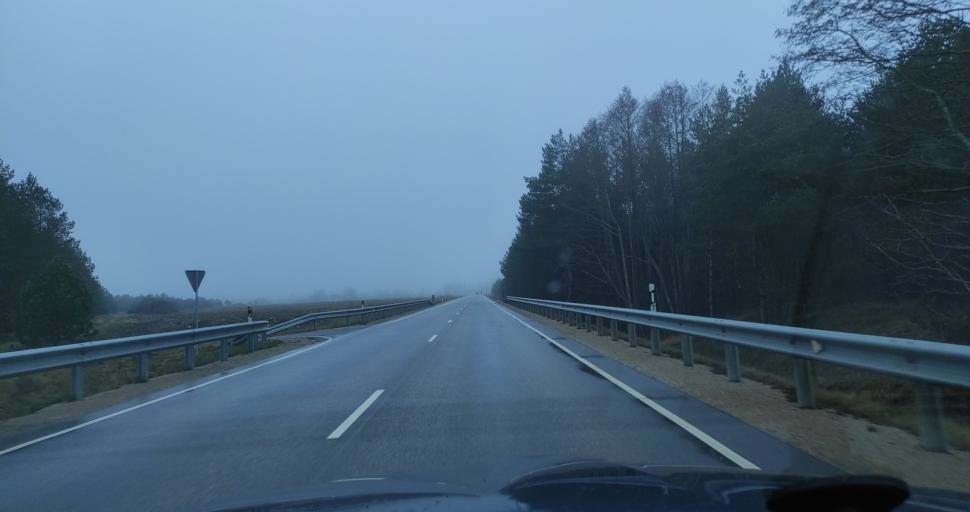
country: LV
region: Pavilostas
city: Pavilosta
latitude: 56.9413
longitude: 21.2833
